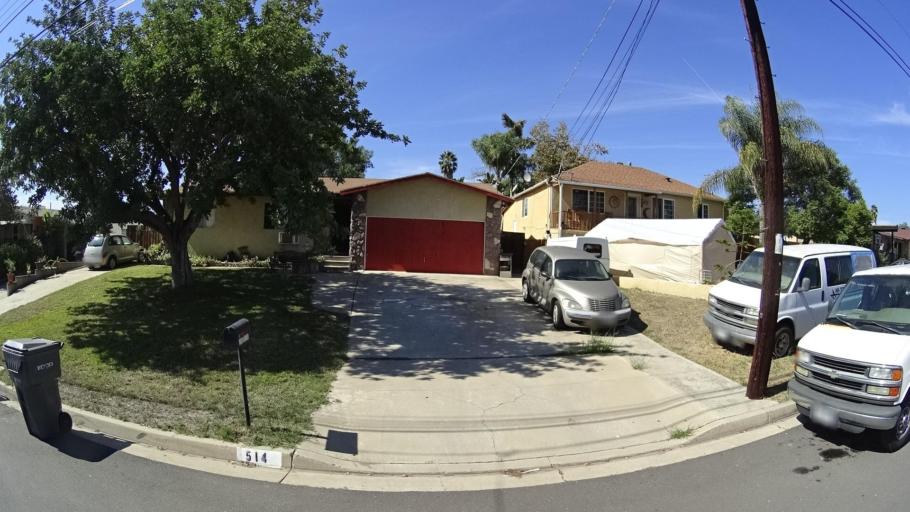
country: US
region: California
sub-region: San Diego County
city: La Presa
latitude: 32.7064
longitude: -116.9941
